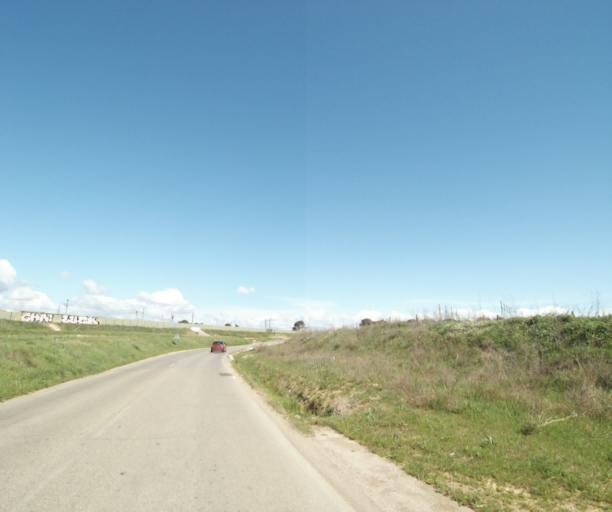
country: FR
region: Languedoc-Roussillon
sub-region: Departement de l'Herault
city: Villeneuve-les-Maguelone
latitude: 43.5668
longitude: 3.8700
